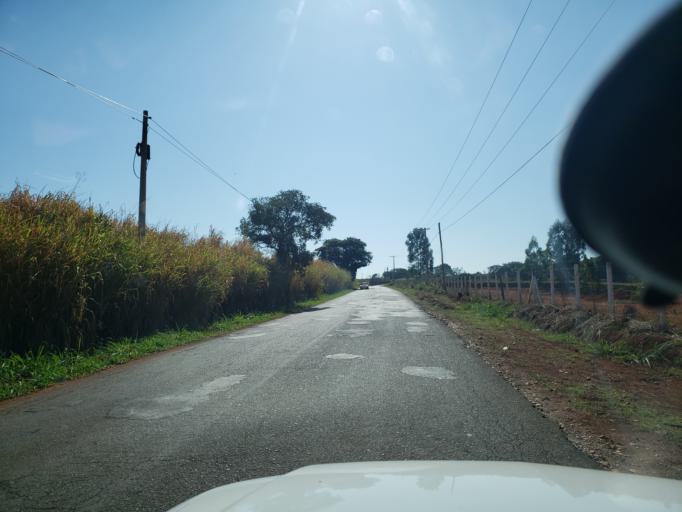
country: BR
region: Sao Paulo
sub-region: Moji-Guacu
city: Mogi-Gaucu
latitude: -22.3467
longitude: -46.8926
